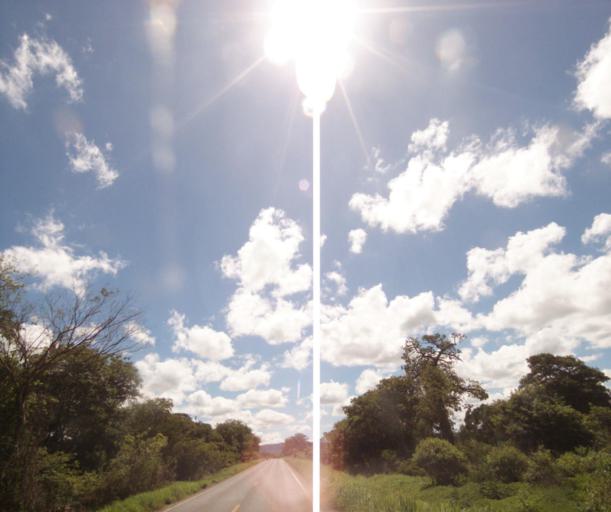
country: BR
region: Bahia
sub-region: Sao Felix Do Coribe
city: Santa Maria da Vitoria
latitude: -13.4072
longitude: -44.1644
